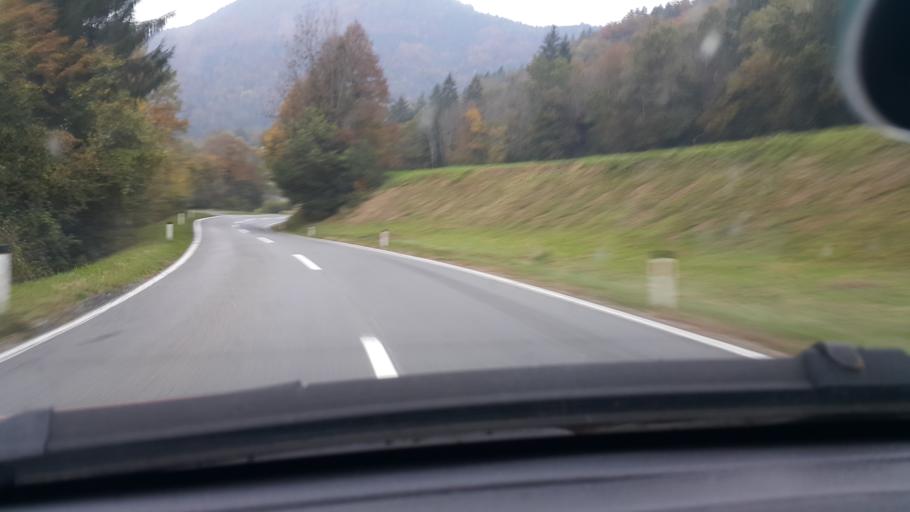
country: AT
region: Carinthia
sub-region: Politischer Bezirk Wolfsberg
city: Sankt Paul im Levanttal
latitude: 46.6686
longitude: 14.8565
